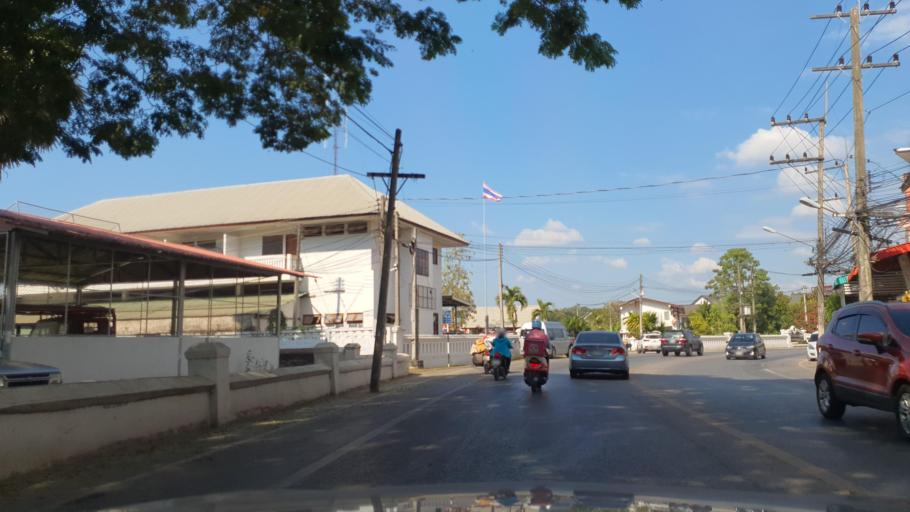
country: TH
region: Nan
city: Nan
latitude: 18.7848
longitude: 100.7746
